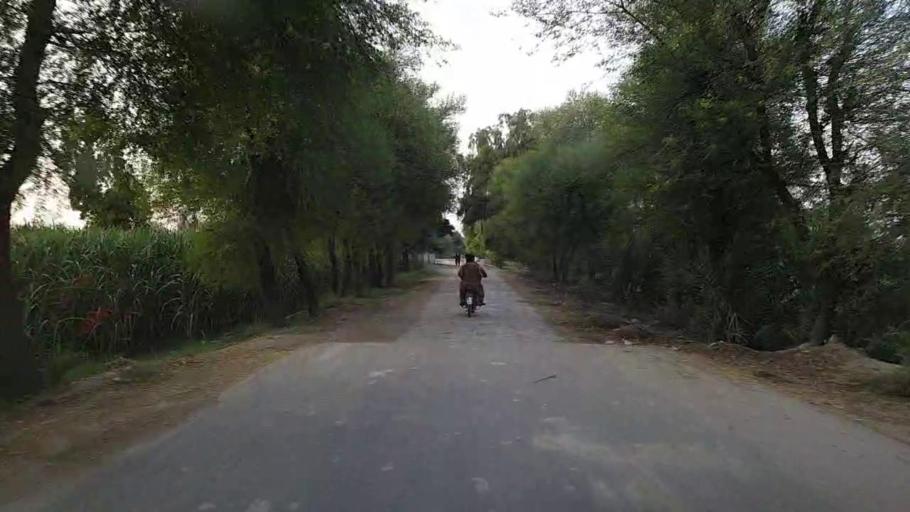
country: PK
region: Sindh
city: Ubauro
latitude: 28.2886
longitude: 69.8000
